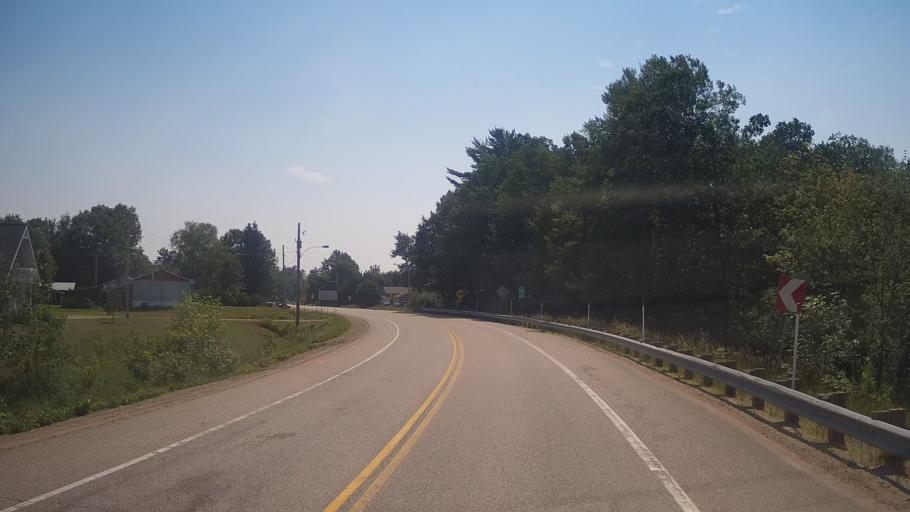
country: CA
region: Quebec
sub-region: Outaouais
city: Fort-Coulonge
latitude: 45.9109
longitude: -76.9206
